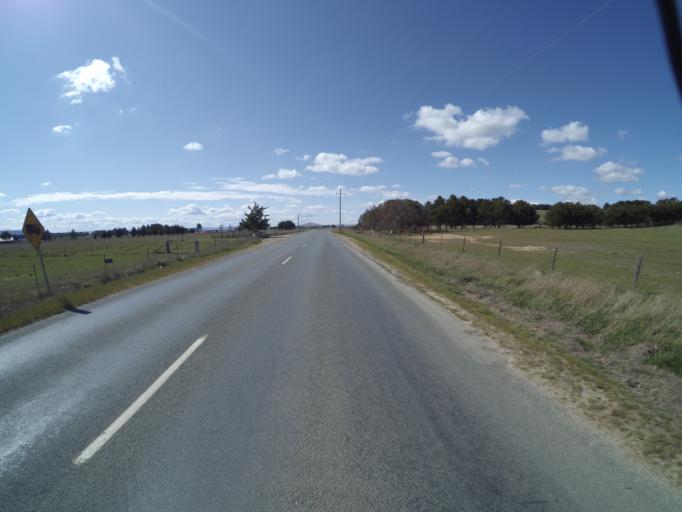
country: AU
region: New South Wales
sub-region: Palerang
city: Bungendore
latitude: -35.2335
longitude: 149.4458
